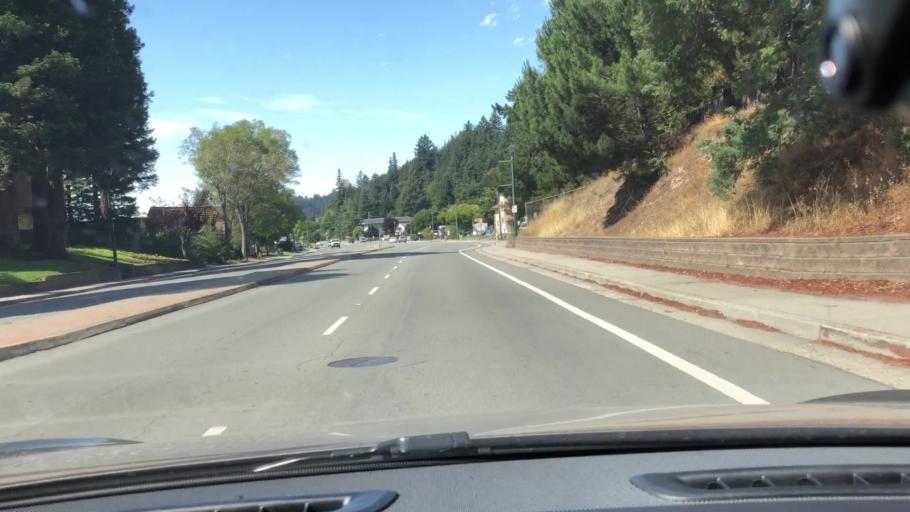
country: US
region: California
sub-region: Santa Cruz County
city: Scotts Valley
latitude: 37.0612
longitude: -122.0081
